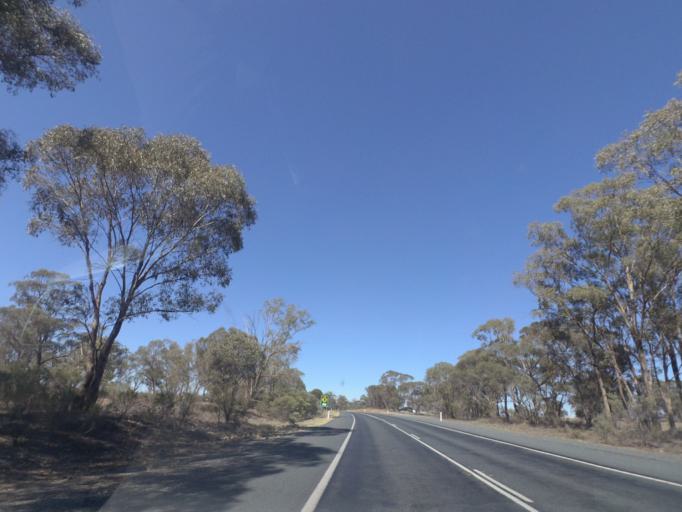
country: AU
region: New South Wales
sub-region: Bland
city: West Wyalong
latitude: -34.1170
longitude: 147.1312
